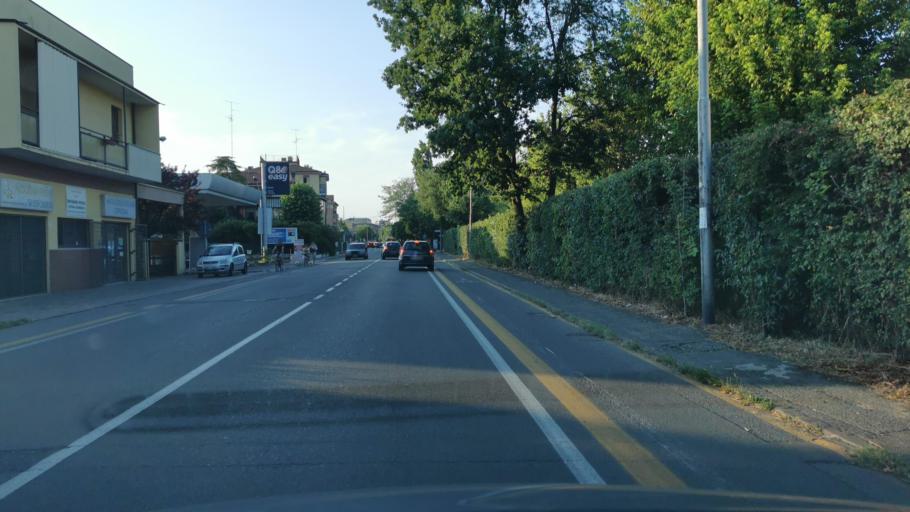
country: IT
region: Emilia-Romagna
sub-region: Provincia di Modena
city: Modena
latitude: 44.6282
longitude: 10.9270
